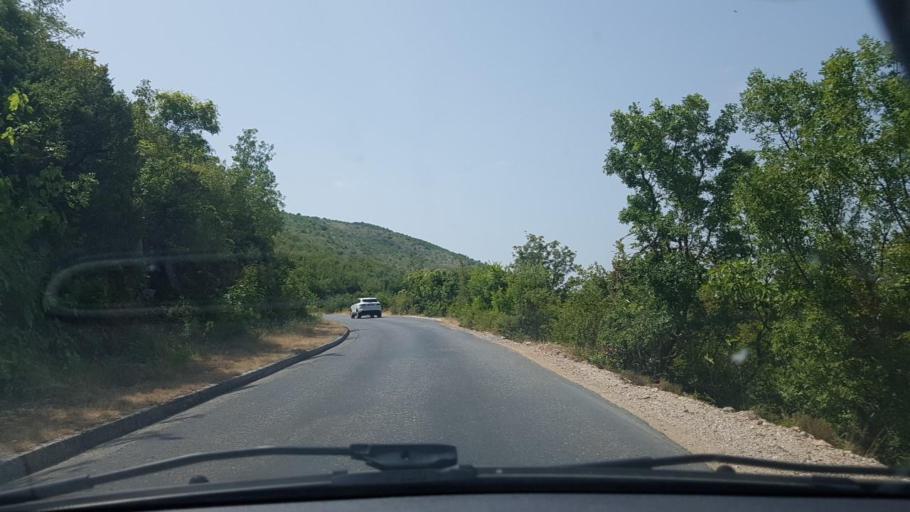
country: HR
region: Dubrovacko-Neretvanska
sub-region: Grad Dubrovnik
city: Metkovic
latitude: 43.0377
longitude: 17.7189
